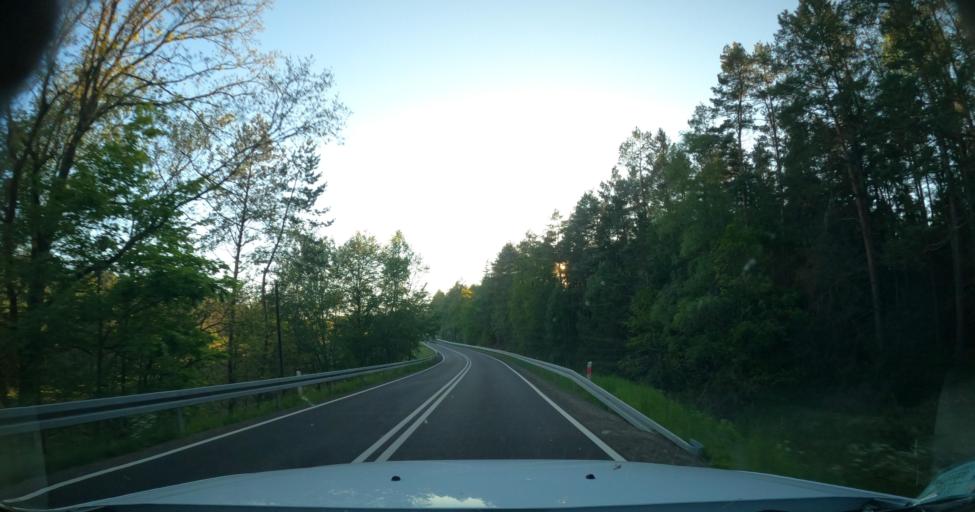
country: PL
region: Pomeranian Voivodeship
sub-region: Powiat bytowski
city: Czarna Dabrowka
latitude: 54.3402
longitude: 17.6170
